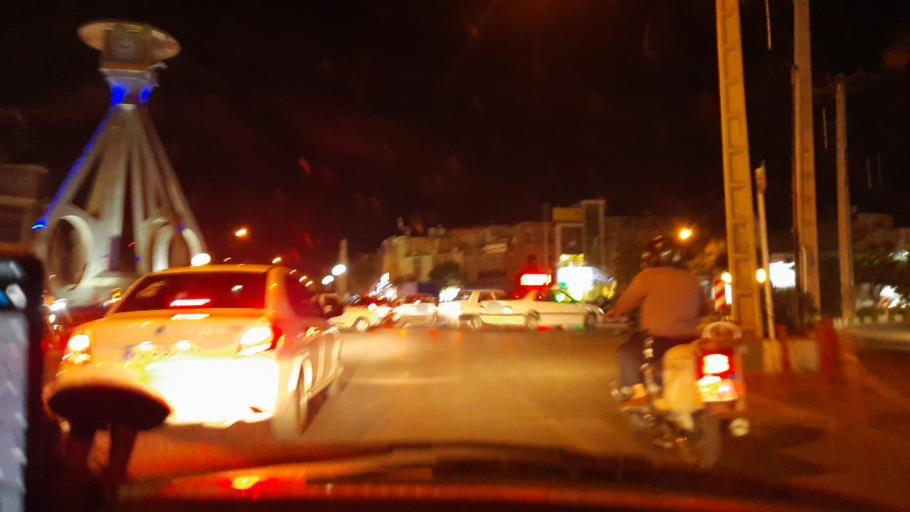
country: IR
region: Markazi
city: Arak
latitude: 34.1053
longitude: 49.6958
